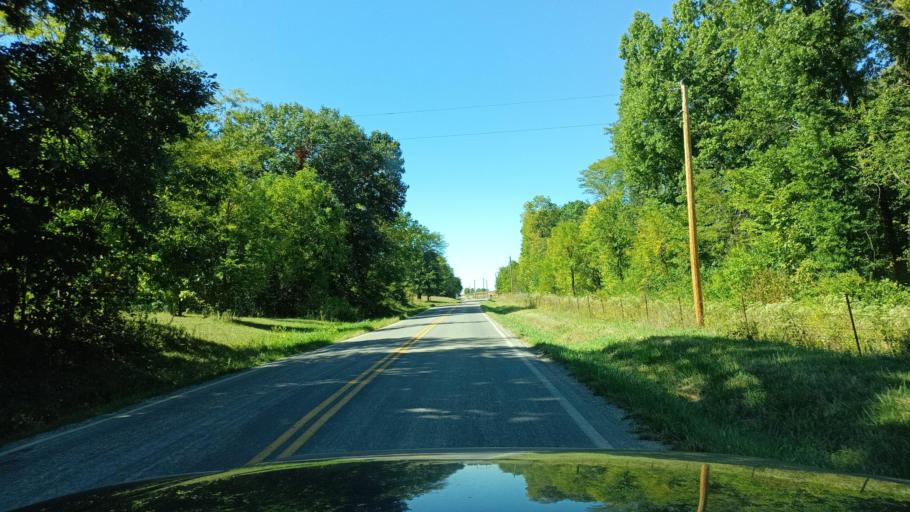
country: US
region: Missouri
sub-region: Macon County
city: La Plata
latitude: 40.0214
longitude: -92.5082
